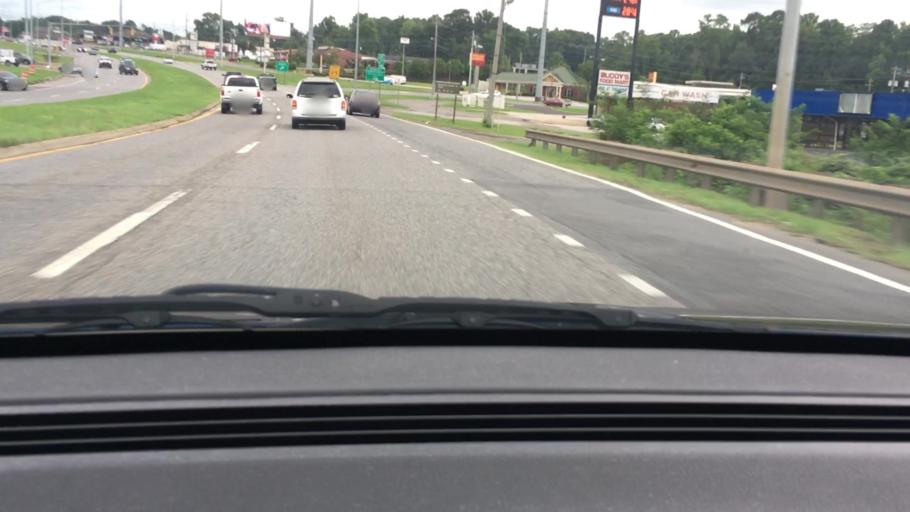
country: US
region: Alabama
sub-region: Tuscaloosa County
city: Tuscaloosa
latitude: 33.2269
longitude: -87.5327
